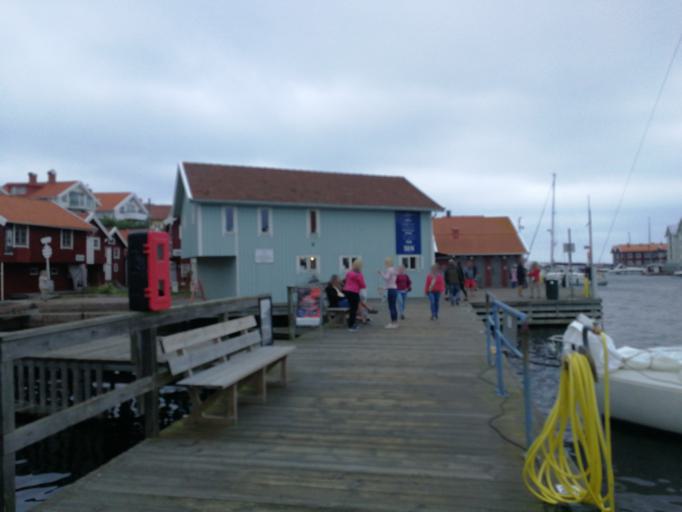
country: SE
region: Vaestra Goetaland
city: Smoegen
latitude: 58.3535
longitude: 11.2224
